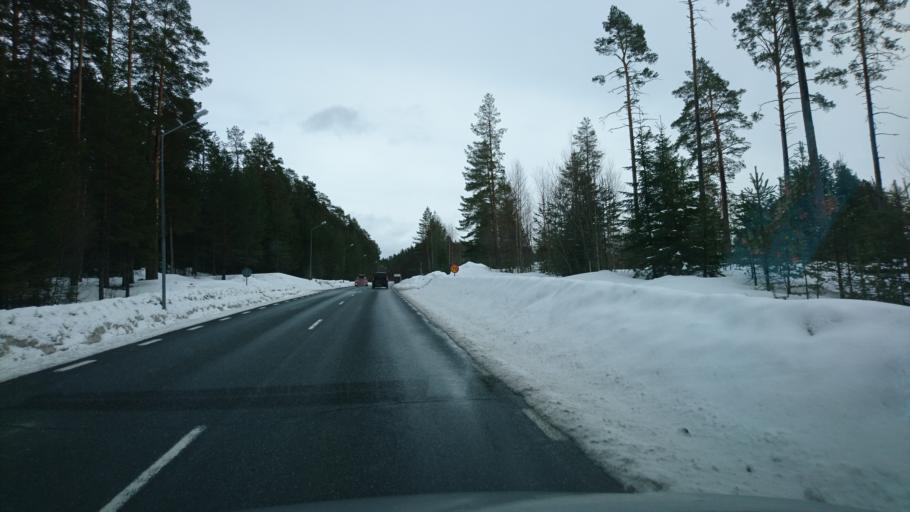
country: SE
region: Vaesternorrland
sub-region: Solleftea Kommun
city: Solleftea
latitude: 63.0680
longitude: 17.0035
